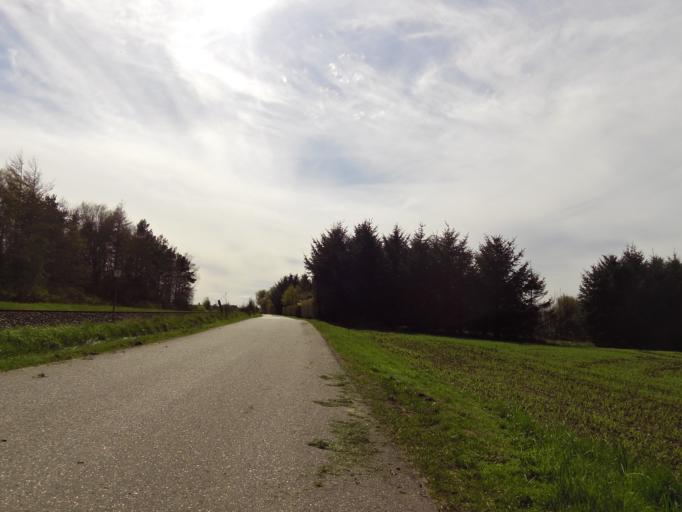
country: DK
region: Central Jutland
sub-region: Skive Kommune
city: Skive
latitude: 56.5579
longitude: 8.9672
